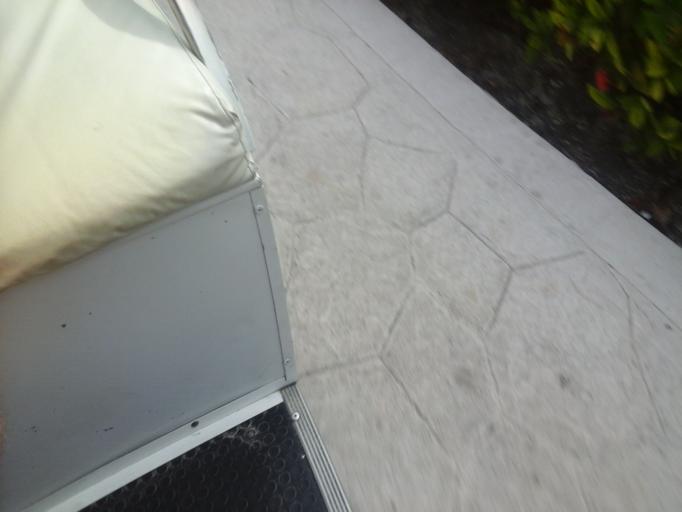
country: MX
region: Quintana Roo
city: Playa del Carmen
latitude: 20.7021
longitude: -87.0154
